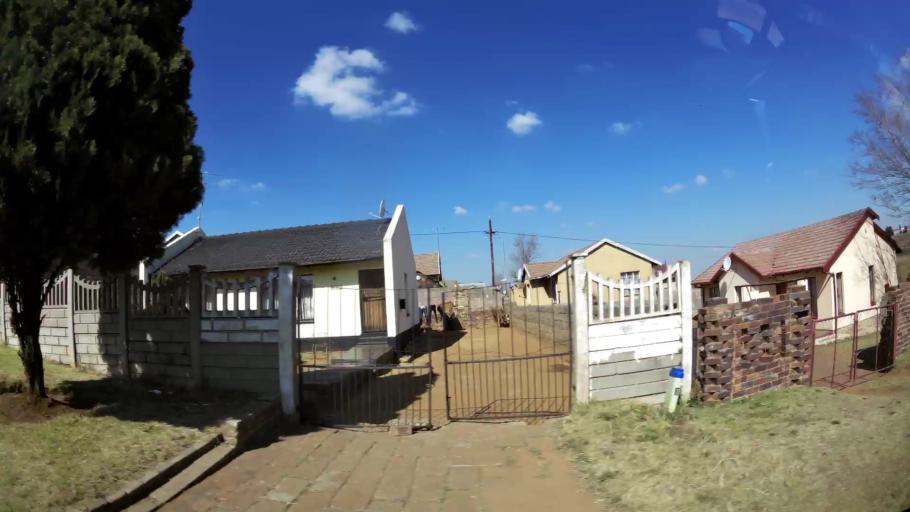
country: ZA
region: Gauteng
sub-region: West Rand District Municipality
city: Randfontein
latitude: -26.1558
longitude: 27.7655
